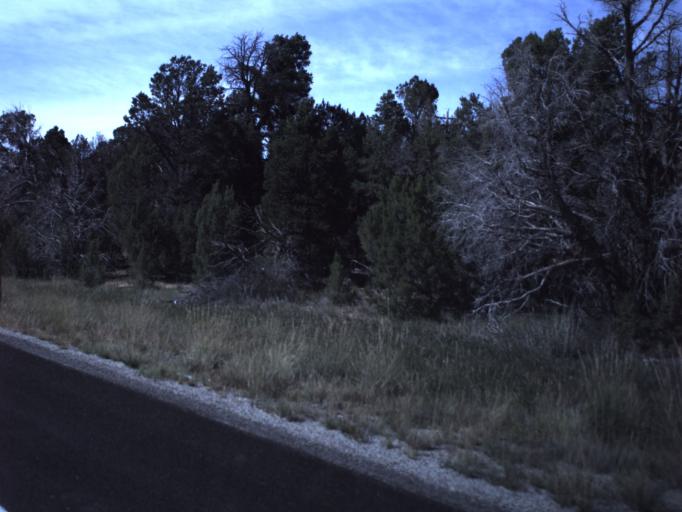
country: US
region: Utah
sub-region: San Juan County
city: Monticello
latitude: 37.8590
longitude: -109.2028
